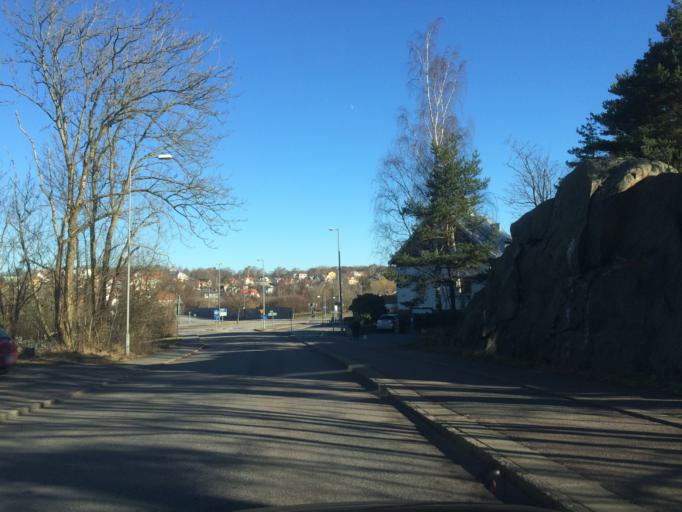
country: SE
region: Vaestra Goetaland
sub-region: Goteborg
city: Majorna
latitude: 57.6754
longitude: 11.8974
